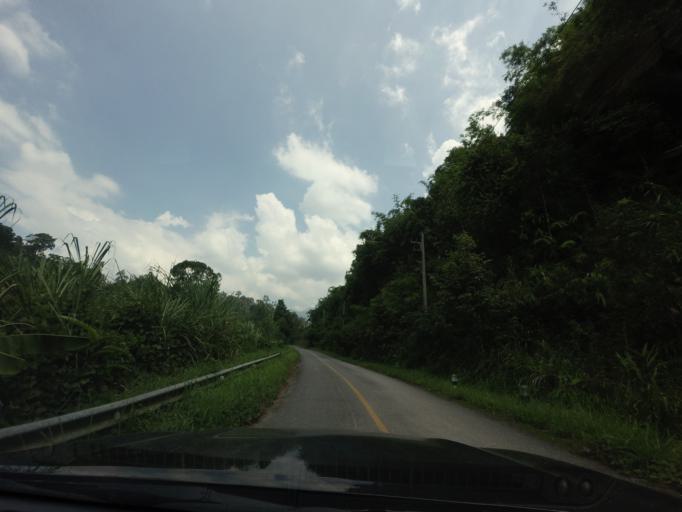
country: TH
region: Uttaradit
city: Nam Pat
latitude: 17.6946
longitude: 100.9313
